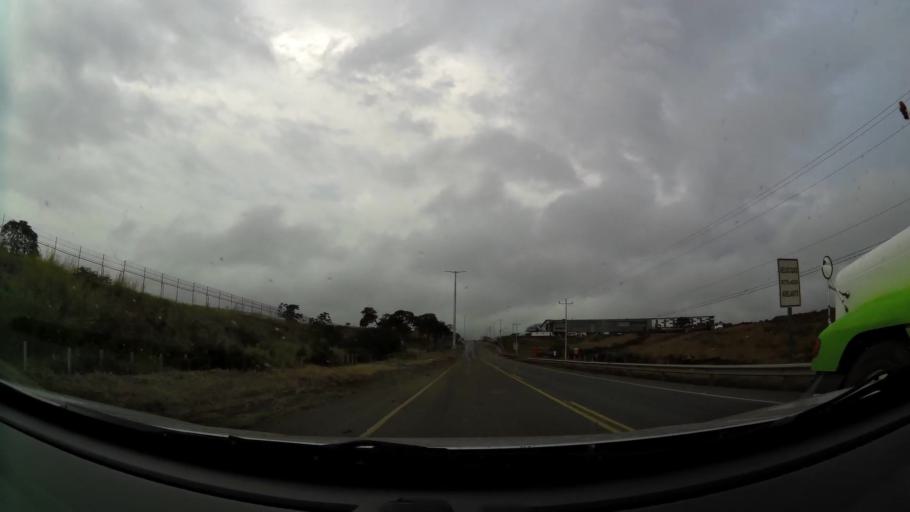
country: CR
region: Alajuela
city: Carrillos
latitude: 9.9733
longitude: -84.2786
